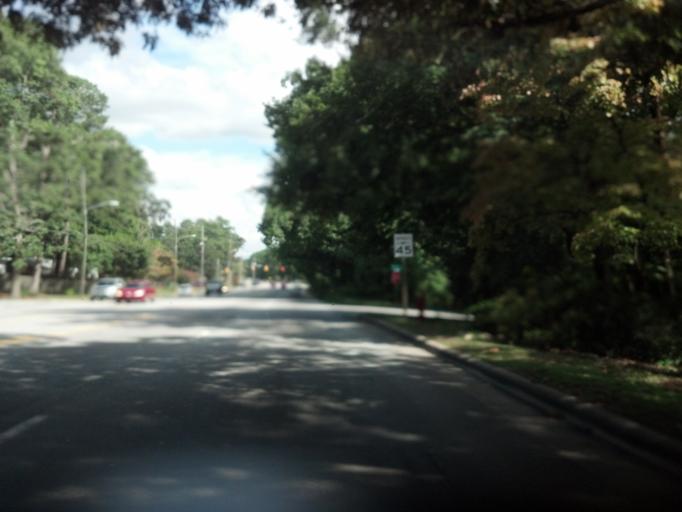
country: US
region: North Carolina
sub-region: Pitt County
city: Greenville
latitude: 35.5904
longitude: -77.3632
